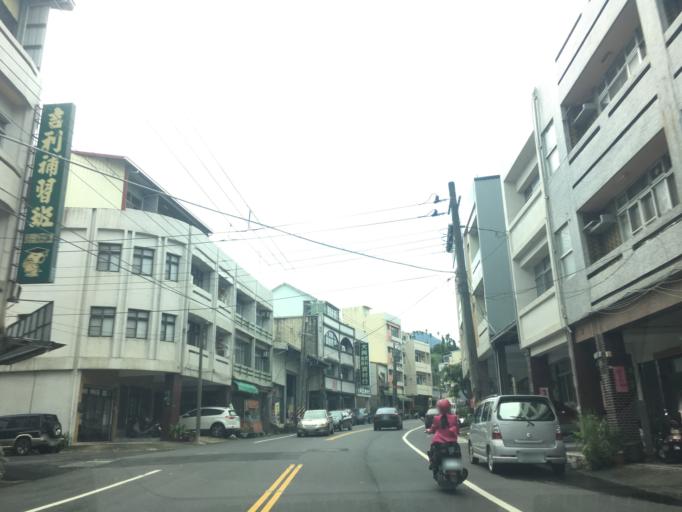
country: TW
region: Taiwan
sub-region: Yunlin
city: Douliu
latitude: 23.5830
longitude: 120.5607
